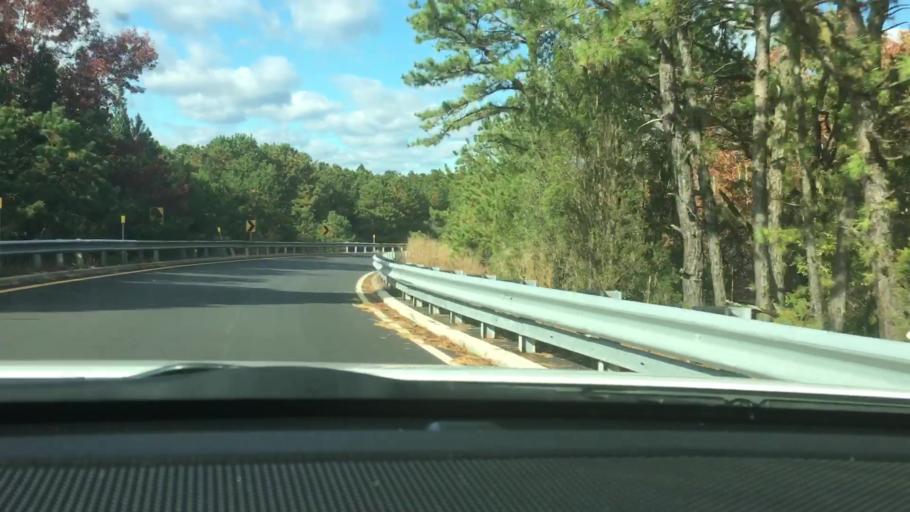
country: US
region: New Jersey
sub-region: Atlantic County
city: Pleasantville
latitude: 39.4148
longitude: -74.5547
